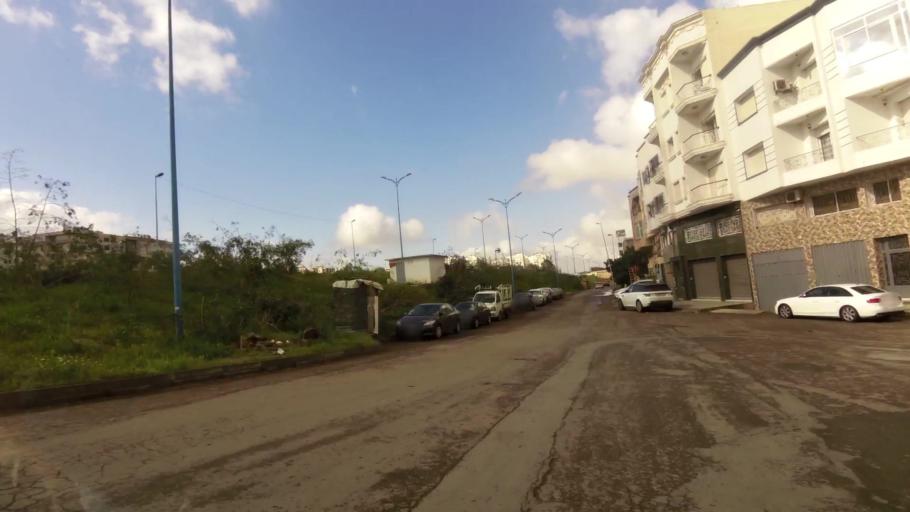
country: MA
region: Grand Casablanca
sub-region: Casablanca
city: Casablanca
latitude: 33.5369
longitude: -7.6816
